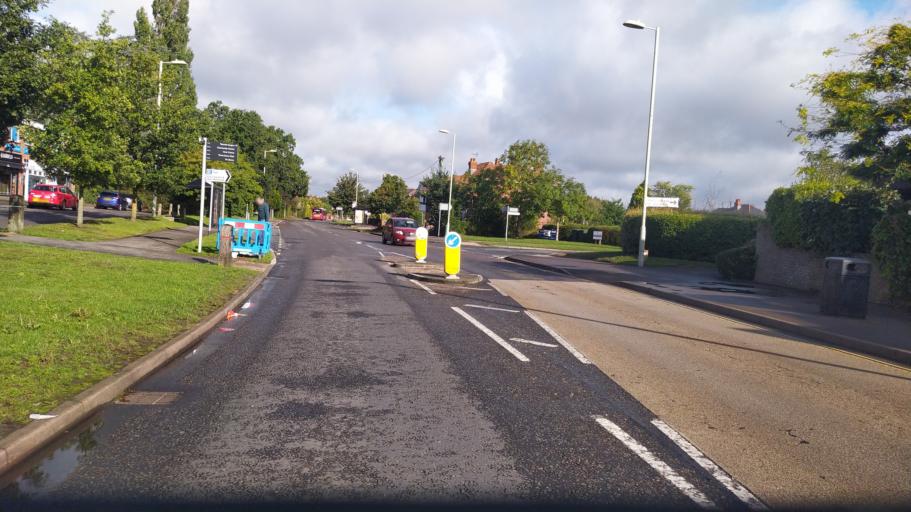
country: GB
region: England
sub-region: Hampshire
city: Totton
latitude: 50.9195
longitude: -1.4905
